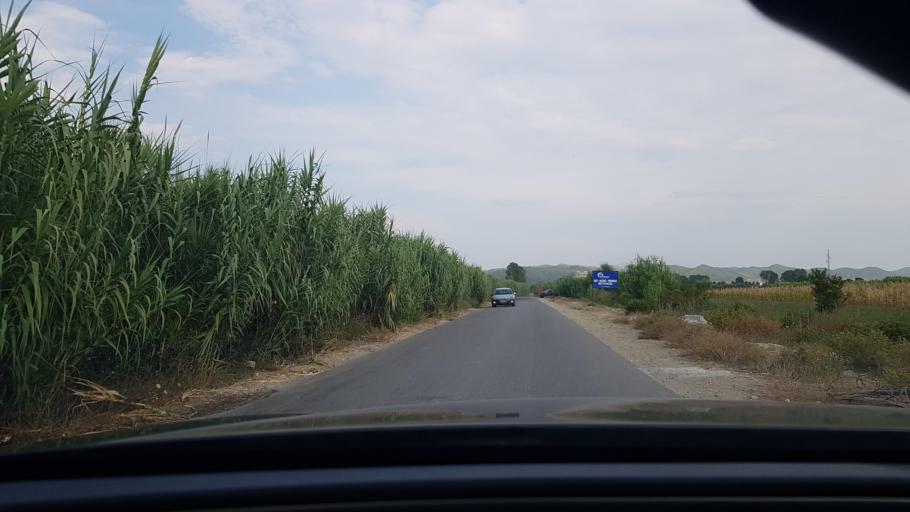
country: AL
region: Durres
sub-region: Rrethi i Durresit
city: Manze
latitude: 41.4834
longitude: 19.5348
